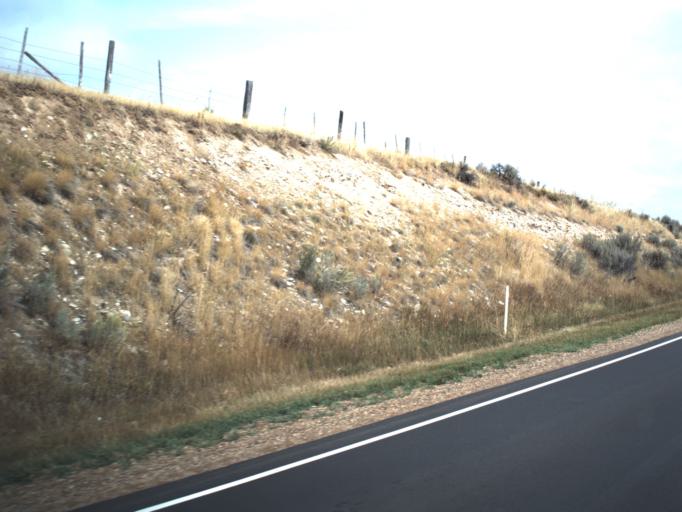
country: US
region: Utah
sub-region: Rich County
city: Randolph
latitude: 41.7001
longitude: -111.1632
